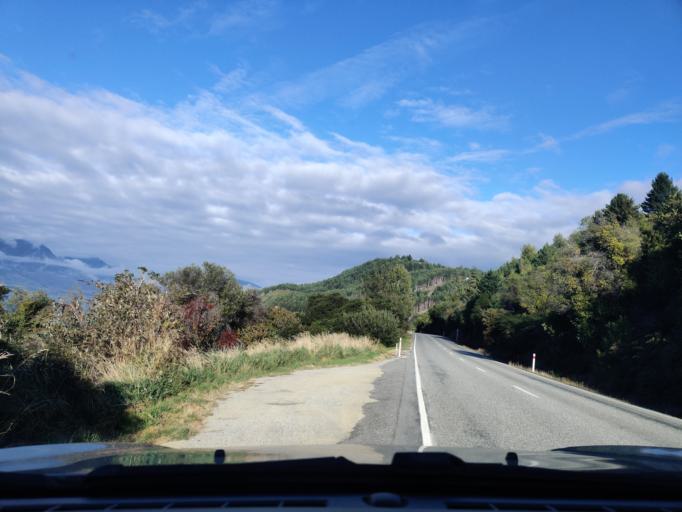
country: NZ
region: Otago
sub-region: Queenstown-Lakes District
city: Queenstown
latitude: -45.0568
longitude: 168.5986
